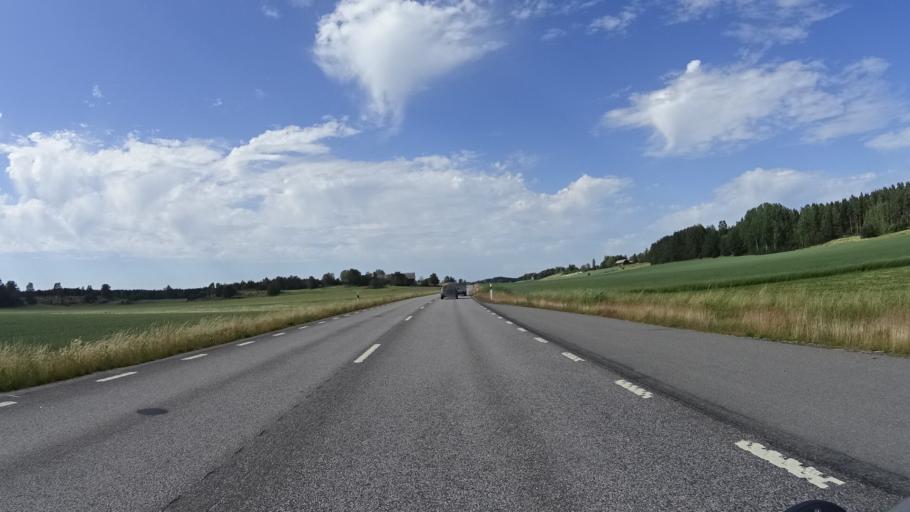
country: SE
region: OEstergoetland
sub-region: Linkopings Kommun
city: Sturefors
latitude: 58.3351
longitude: 15.8504
